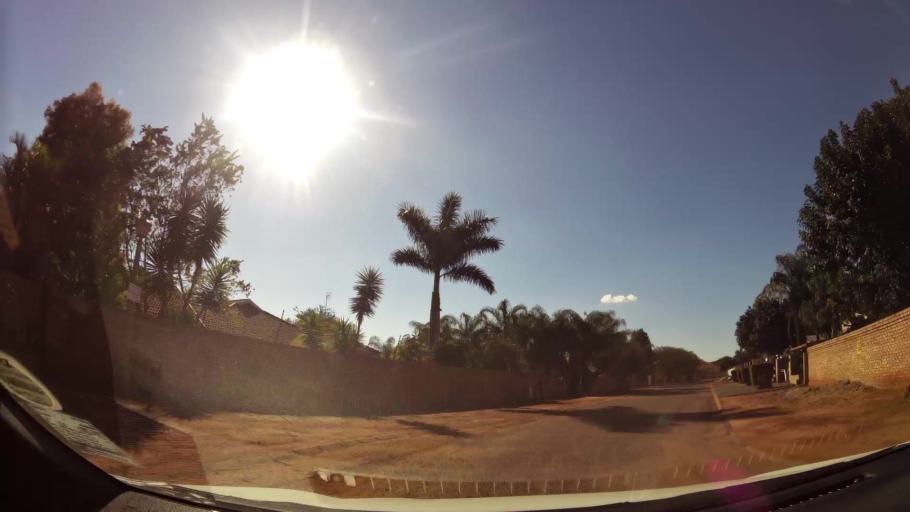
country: ZA
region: Limpopo
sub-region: Waterberg District Municipality
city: Mokopane
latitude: -24.2086
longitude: 28.9909
